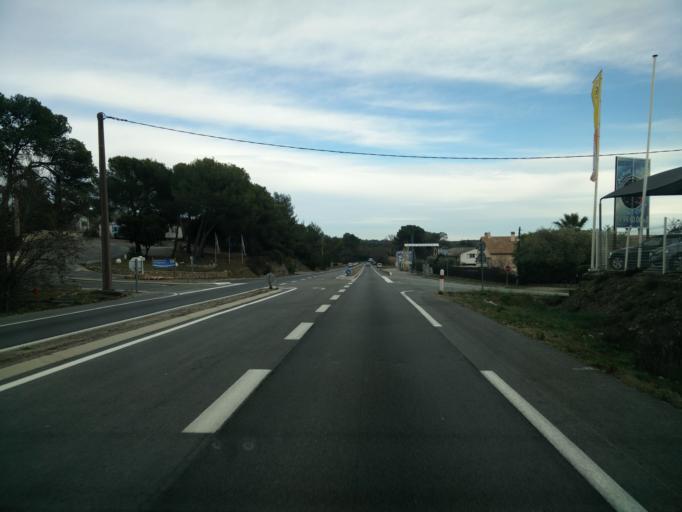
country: FR
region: Provence-Alpes-Cote d'Azur
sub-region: Departement du Var
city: Le Muy
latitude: 43.4680
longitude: 6.5913
